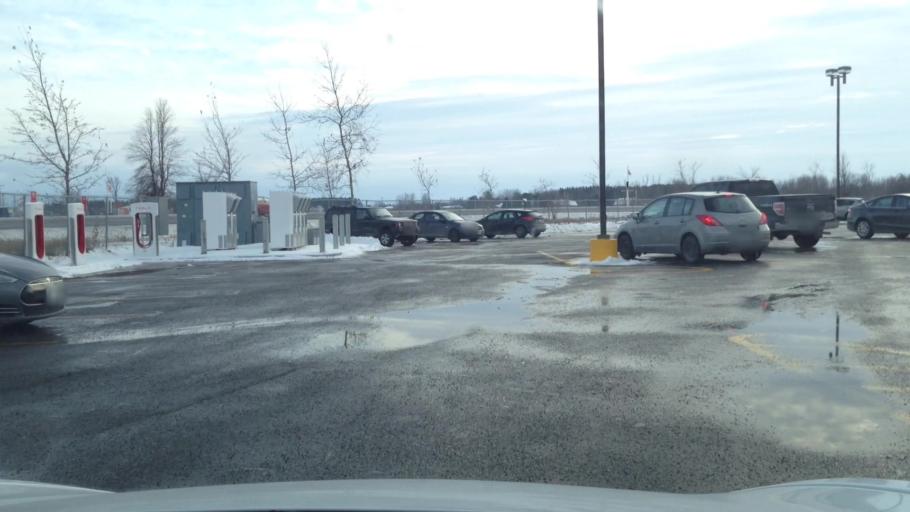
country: CA
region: Ontario
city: Casselman
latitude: 45.3047
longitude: -75.0819
